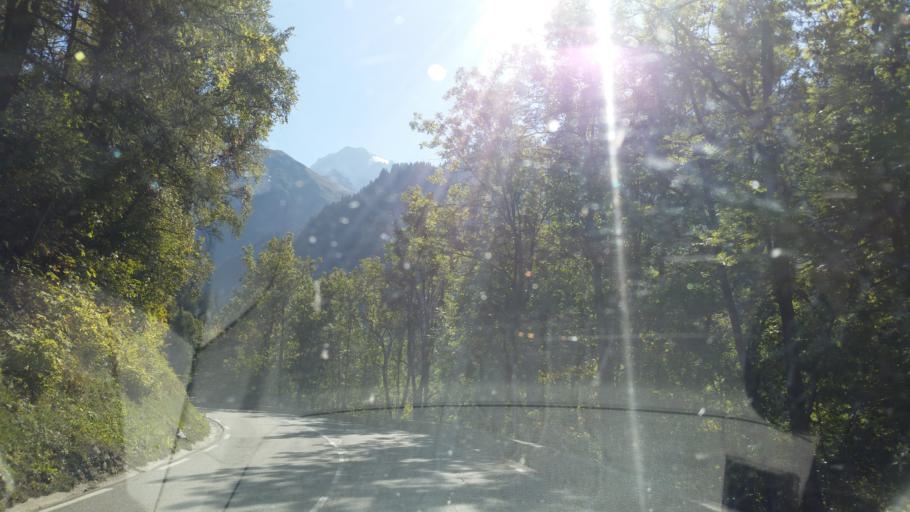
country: FR
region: Rhone-Alpes
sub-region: Departement de la Savoie
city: Seez
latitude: 45.5831
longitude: 6.8844
